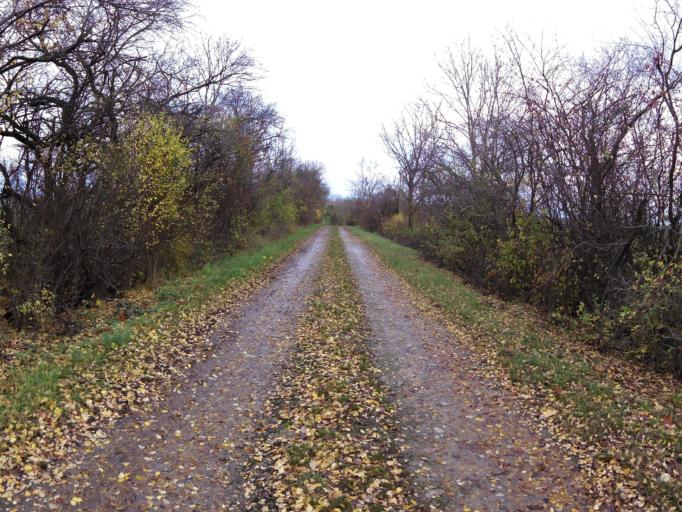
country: DE
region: Thuringia
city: Ifta
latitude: 51.0579
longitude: 10.1319
